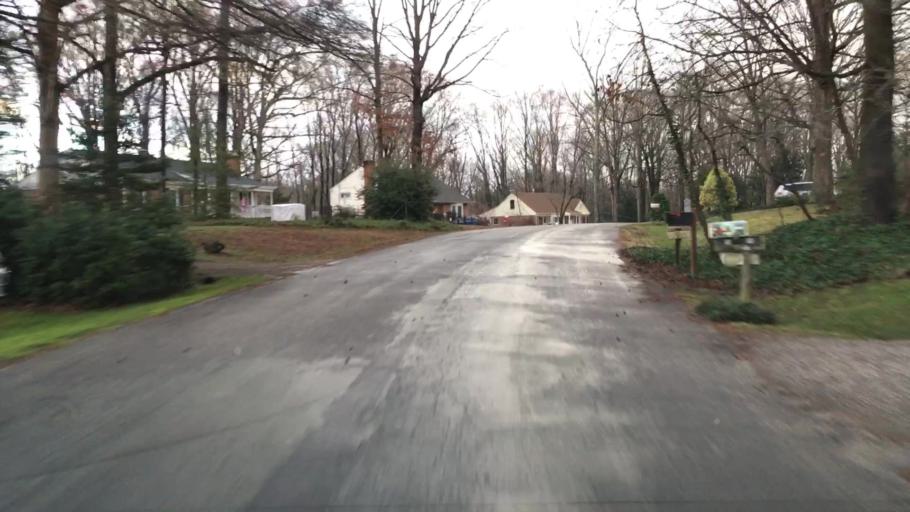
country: US
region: Virginia
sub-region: Chesterfield County
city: Bon Air
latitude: 37.5182
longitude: -77.6251
